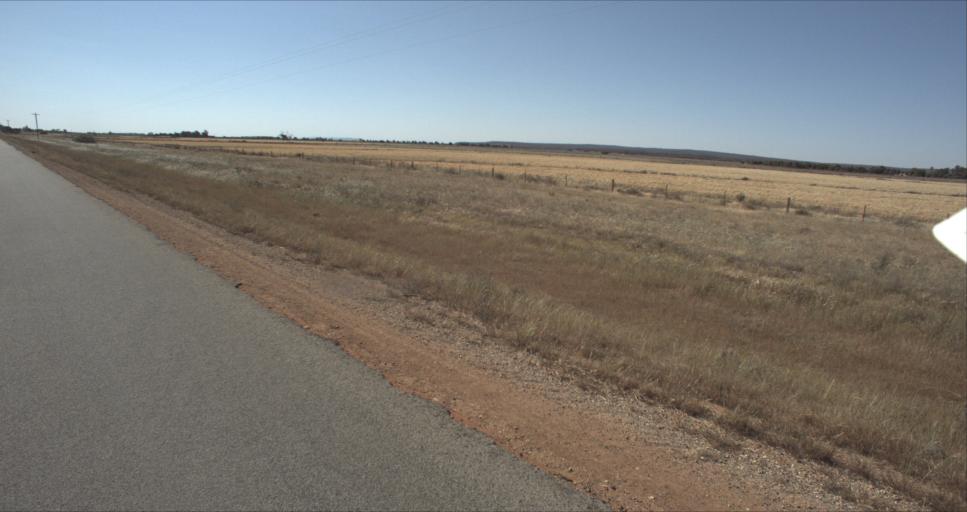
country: AU
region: New South Wales
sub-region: Leeton
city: Leeton
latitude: -34.4951
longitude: 146.3881
